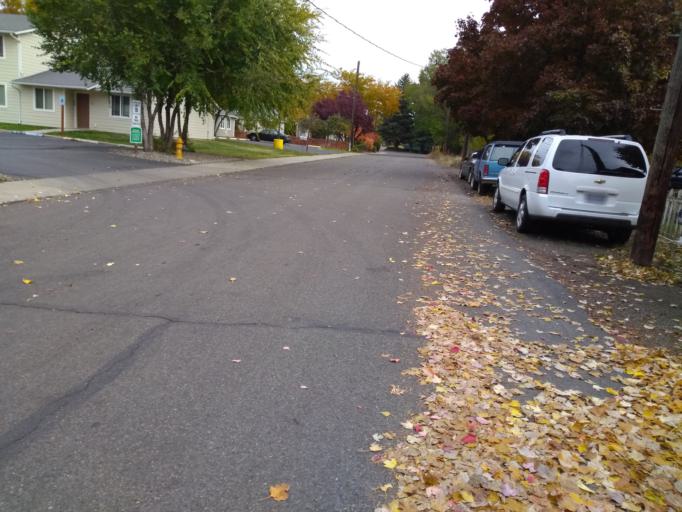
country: US
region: Washington
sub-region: Kittitas County
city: Ellensburg
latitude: 46.9869
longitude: -120.5431
